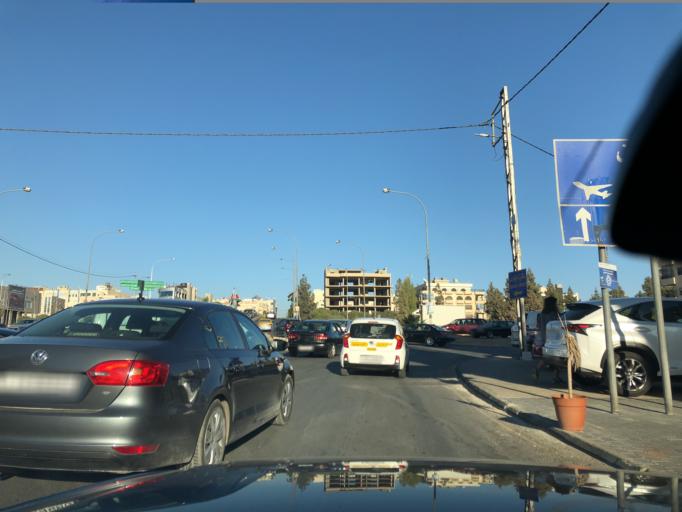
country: JO
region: Amman
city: Wadi as Sir
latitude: 31.9543
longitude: 35.8568
